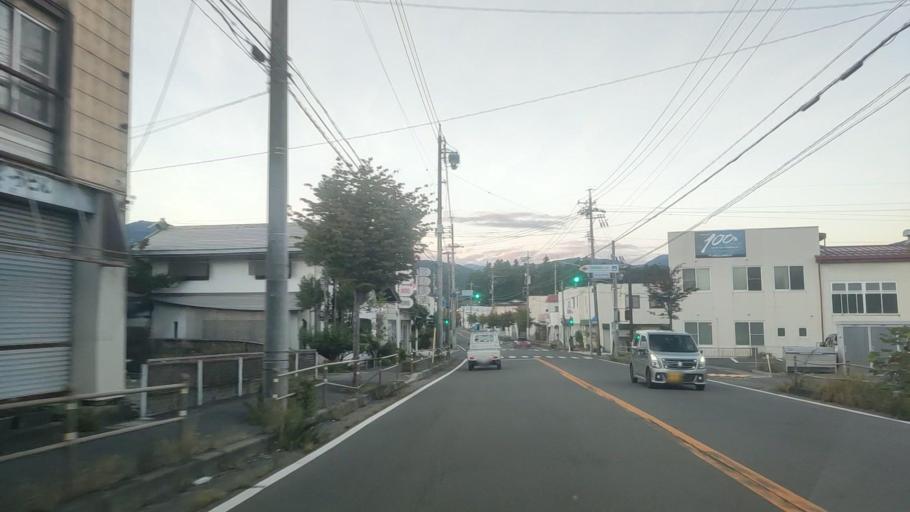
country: JP
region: Nagano
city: Okaya
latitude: 36.0738
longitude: 138.0621
